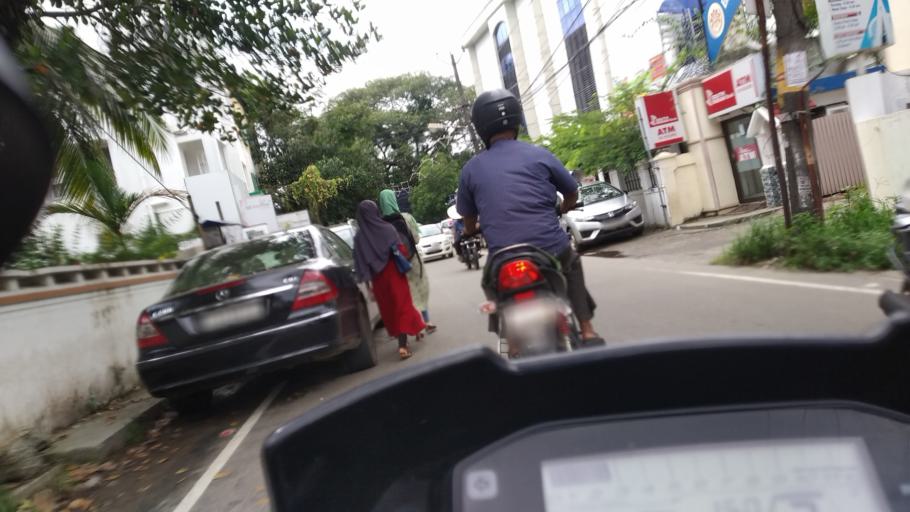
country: IN
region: Kerala
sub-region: Ernakulam
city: Cochin
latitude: 9.9870
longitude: 76.2812
